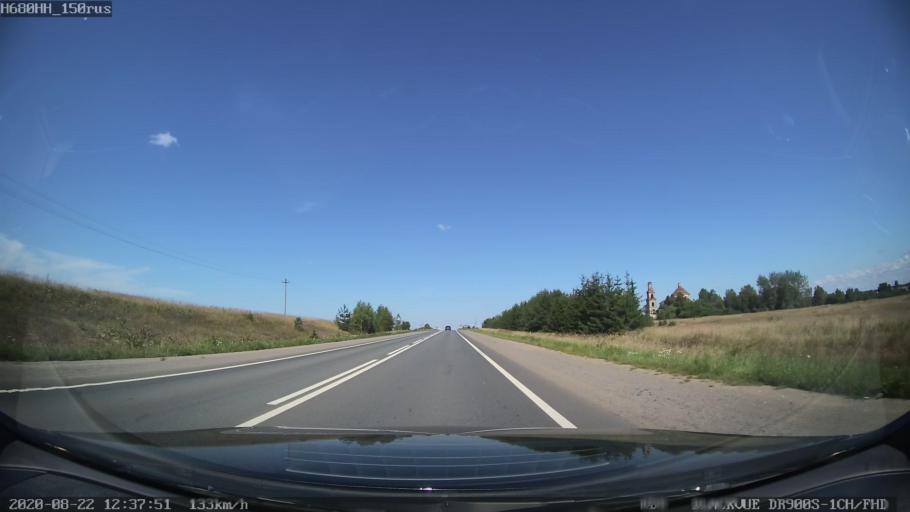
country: RU
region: Tverskaya
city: Rameshki
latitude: 57.3038
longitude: 36.0888
